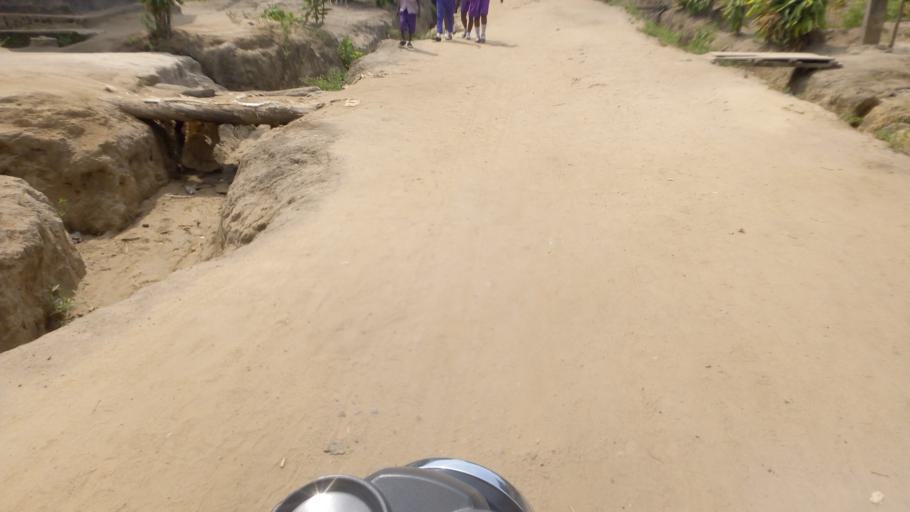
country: SL
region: Western Area
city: Waterloo
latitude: 8.3111
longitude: -13.0636
